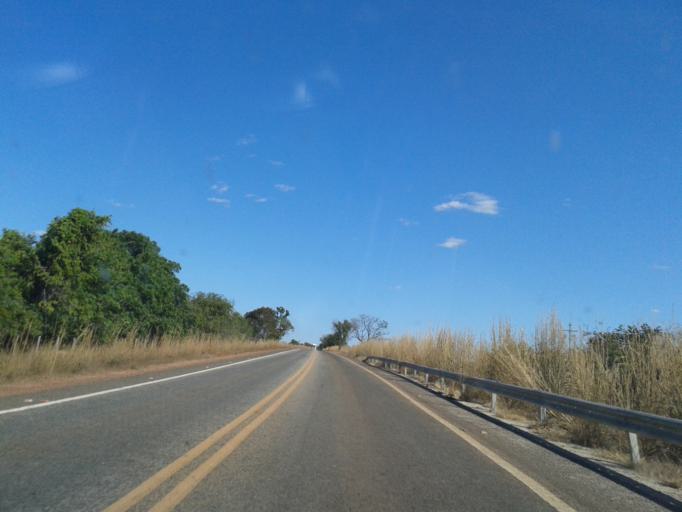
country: BR
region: Goias
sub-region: Mozarlandia
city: Mozarlandia
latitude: -14.4963
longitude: -50.4844
